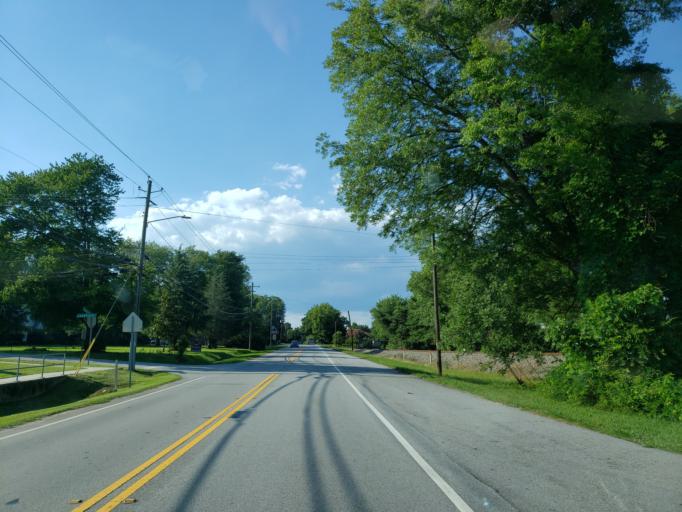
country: US
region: Georgia
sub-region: Haralson County
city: Bremen
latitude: 33.7278
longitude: -85.1489
